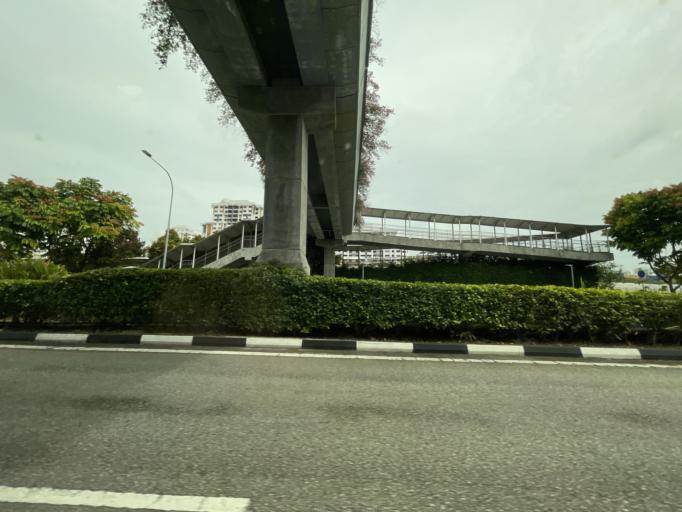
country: SG
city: Singapore
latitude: 1.3363
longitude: 103.7468
